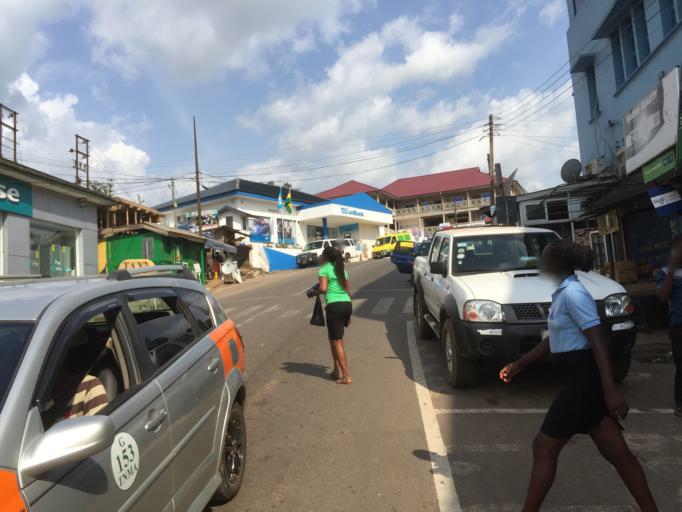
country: GH
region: Western
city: Tarkwa
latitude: 5.3071
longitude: -1.9945
